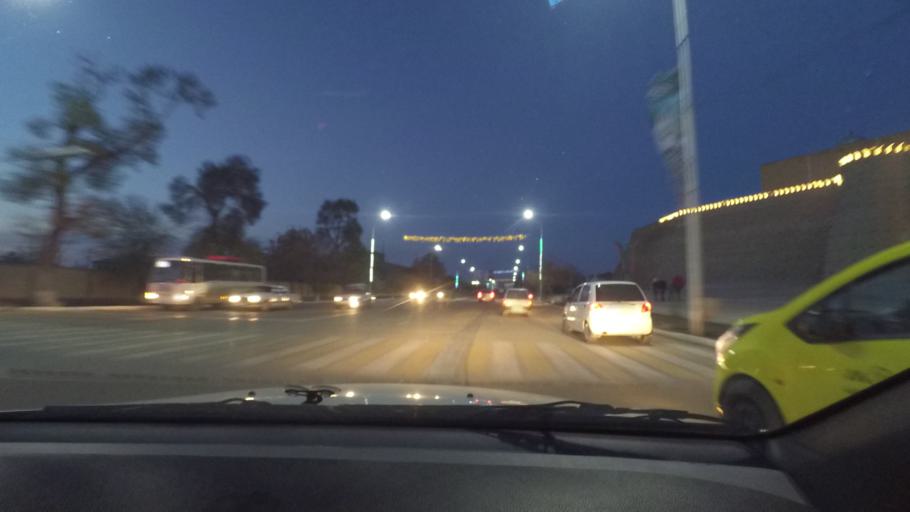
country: UZ
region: Bukhara
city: Bukhara
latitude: 39.7781
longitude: 64.4089
